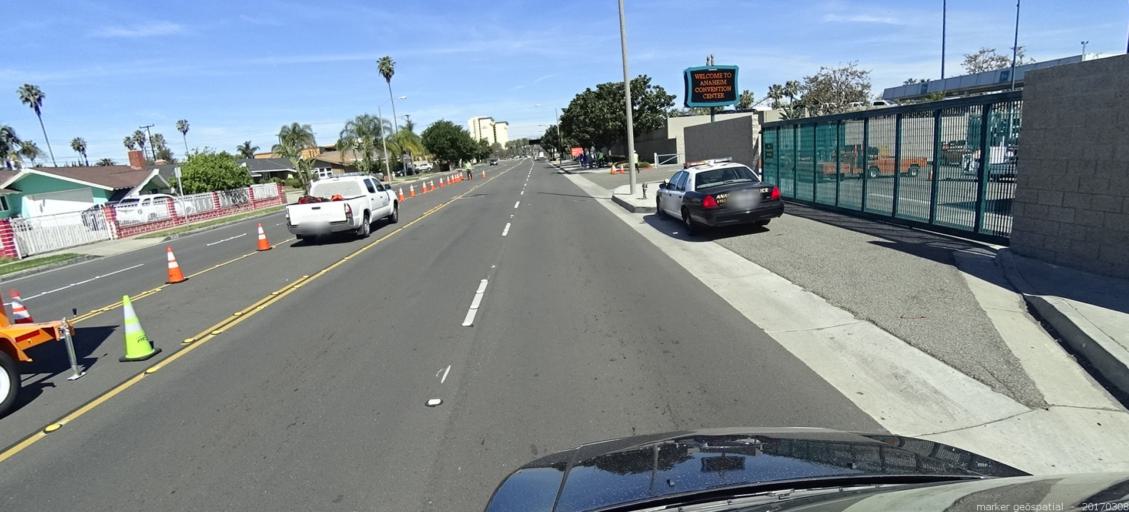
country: US
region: California
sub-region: Orange County
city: Garden Grove
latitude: 33.8002
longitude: -117.9239
